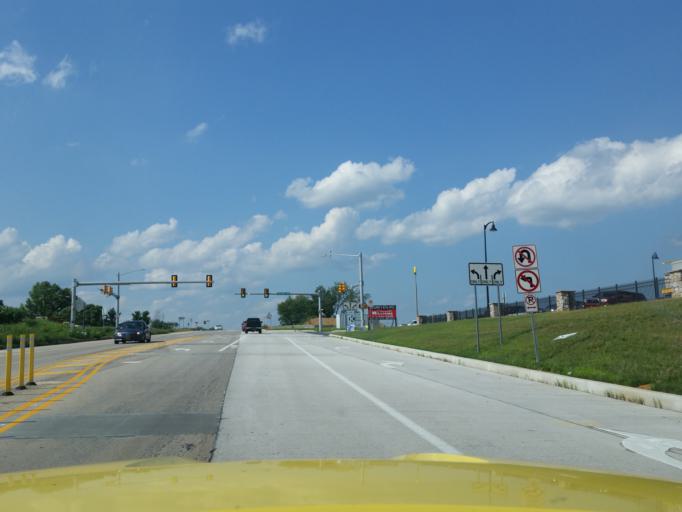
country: US
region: Pennsylvania
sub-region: Lancaster County
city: Salunga
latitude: 40.1124
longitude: -76.4514
